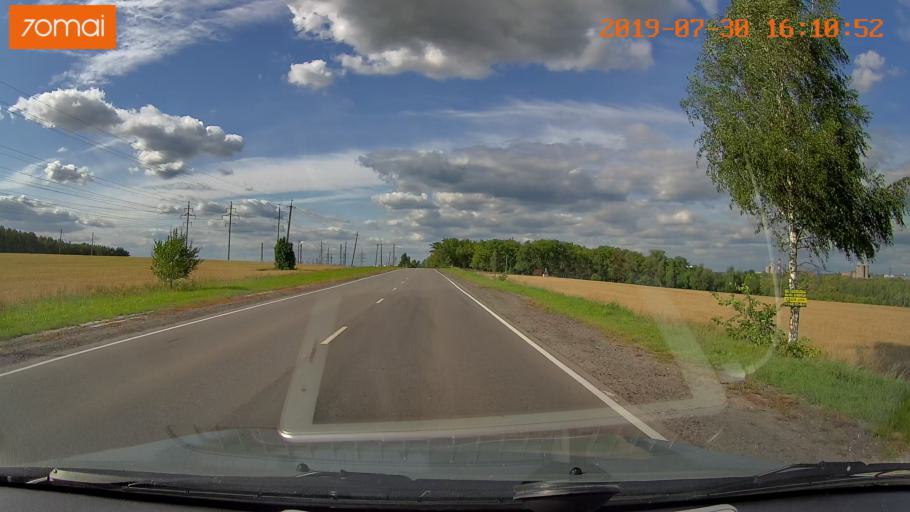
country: RU
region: Moskovskaya
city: Peski
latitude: 55.2680
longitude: 38.7145
